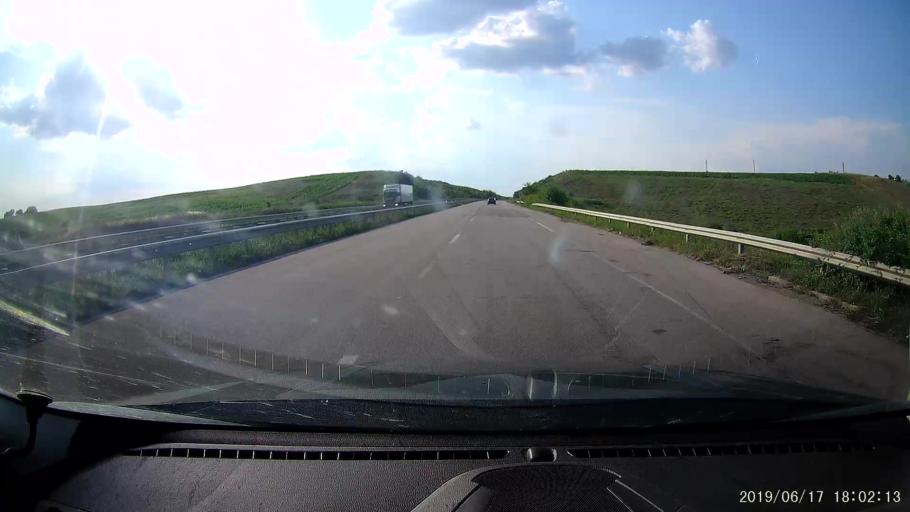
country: BG
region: Khaskovo
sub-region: Obshtina Svilengrad
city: Svilengrad
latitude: 41.7560
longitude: 26.2349
